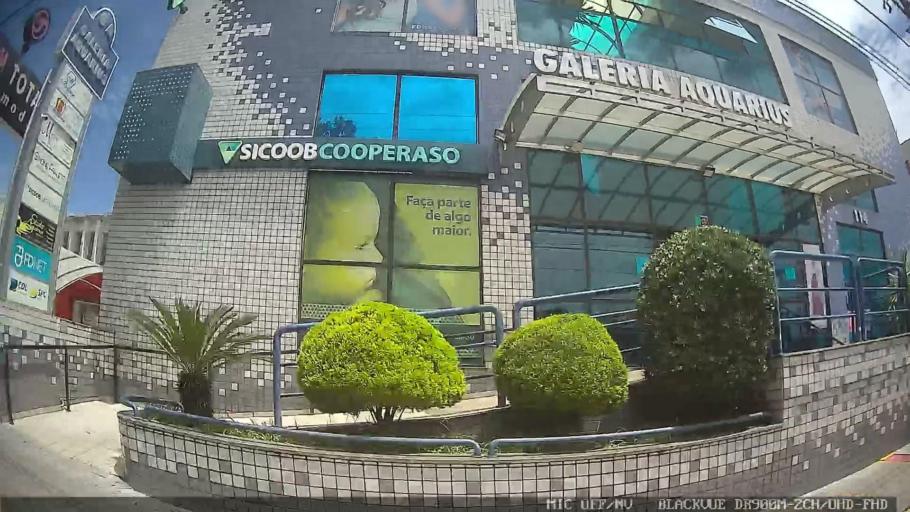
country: BR
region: Sao Paulo
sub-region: Laranjal Paulista
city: Laranjal Paulista
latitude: -23.0517
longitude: -47.8376
